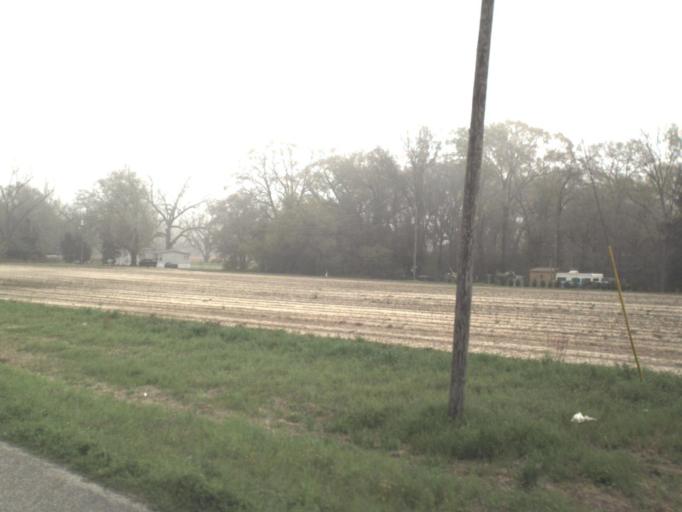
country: US
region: Florida
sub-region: Gadsden County
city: Gretna
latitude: 30.5431
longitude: -84.6769
